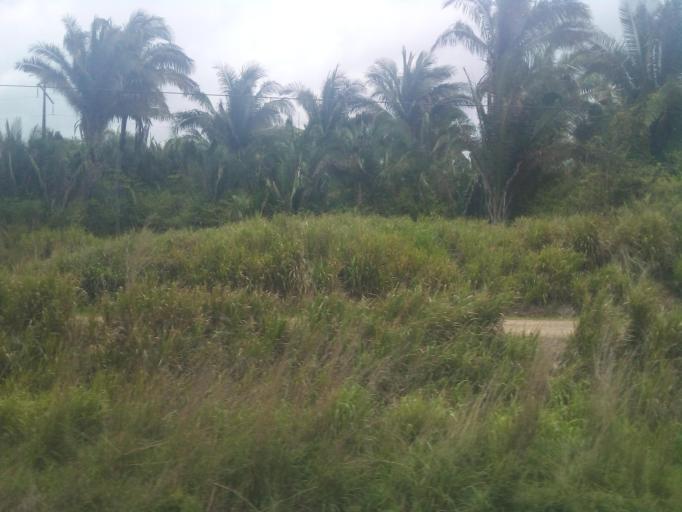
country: BR
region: Maranhao
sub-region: Pindare Mirim
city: Pindare Mirim
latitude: -3.6435
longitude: -45.2214
